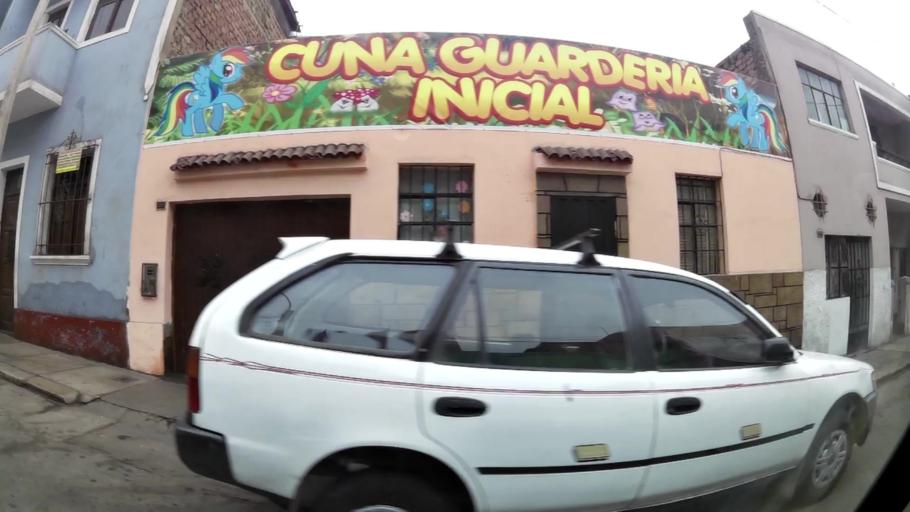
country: PE
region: Lima
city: Lima
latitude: -12.0532
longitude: -77.0509
